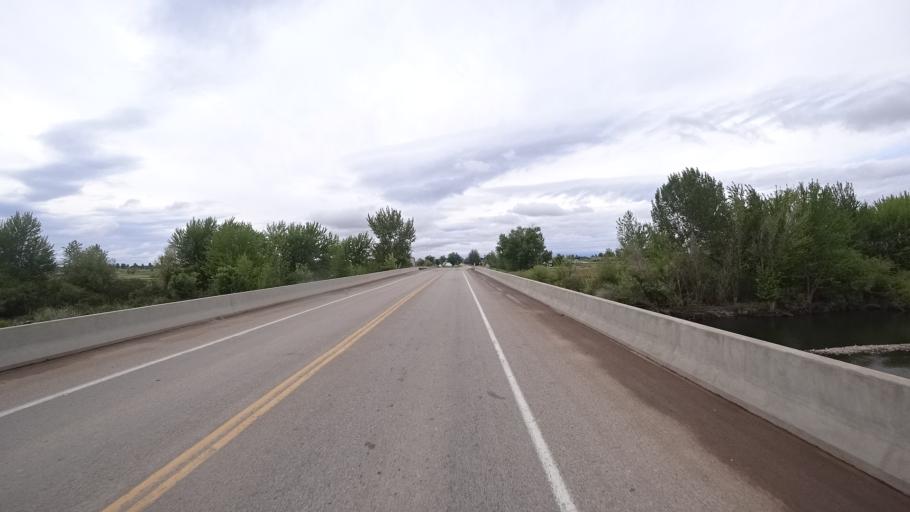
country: US
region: Idaho
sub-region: Ada County
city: Star
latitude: 43.6806
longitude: -116.4932
